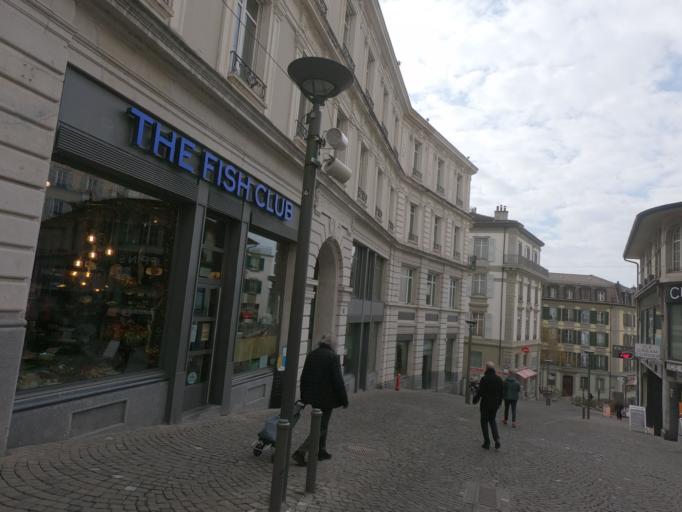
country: CH
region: Vaud
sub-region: Lausanne District
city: Lausanne
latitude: 46.5192
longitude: 6.6319
